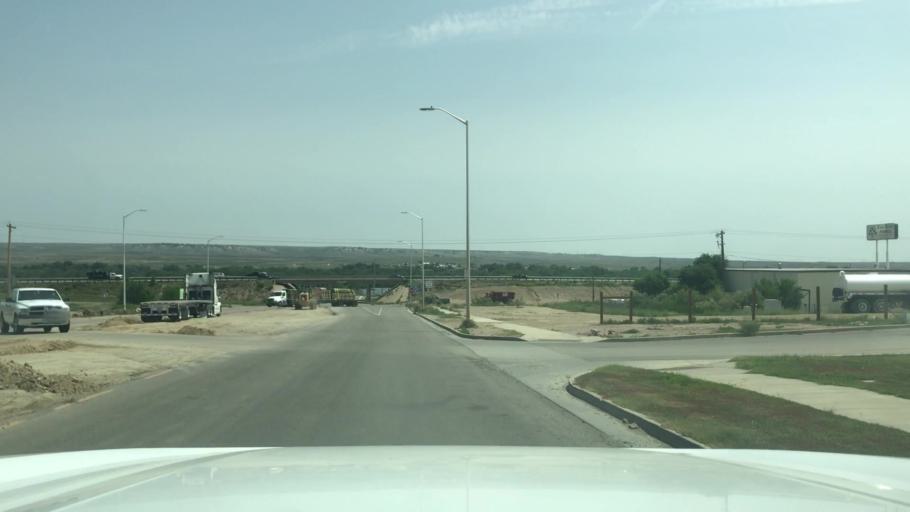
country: US
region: Colorado
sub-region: Pueblo County
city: Pueblo
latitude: 38.3430
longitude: -104.6228
